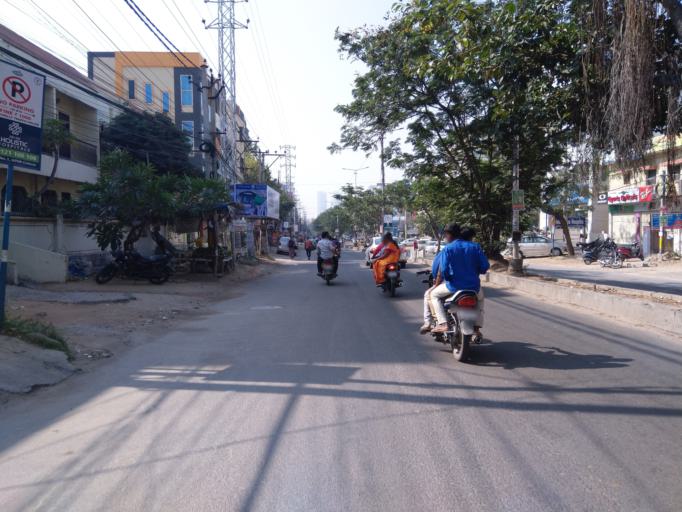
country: IN
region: Telangana
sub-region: Rangareddi
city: Kukatpalli
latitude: 17.4915
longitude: 78.4017
